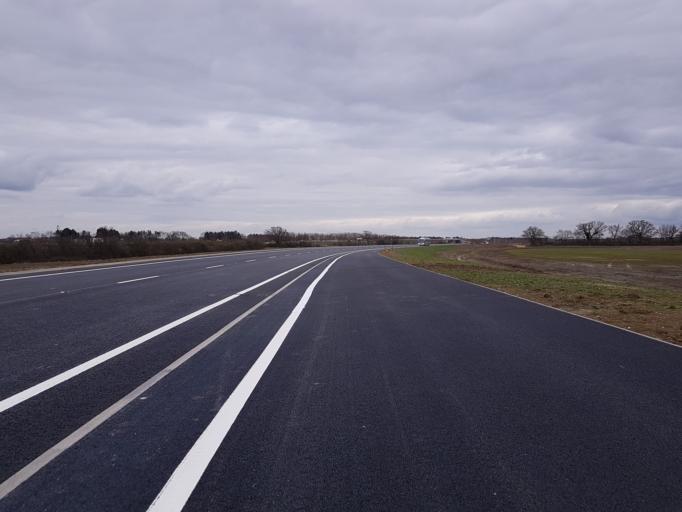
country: GB
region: England
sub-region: Cambridgeshire
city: Girton
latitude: 52.2388
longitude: 0.0535
